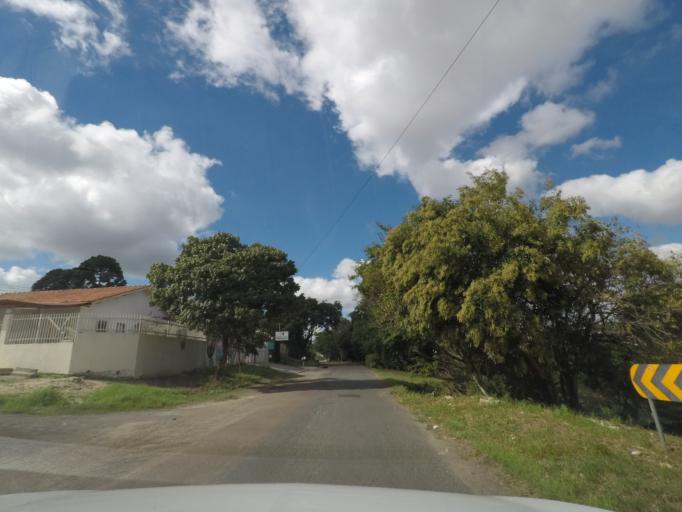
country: BR
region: Parana
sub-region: Sao Jose Dos Pinhais
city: Sao Jose dos Pinhais
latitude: -25.4854
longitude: -49.2347
